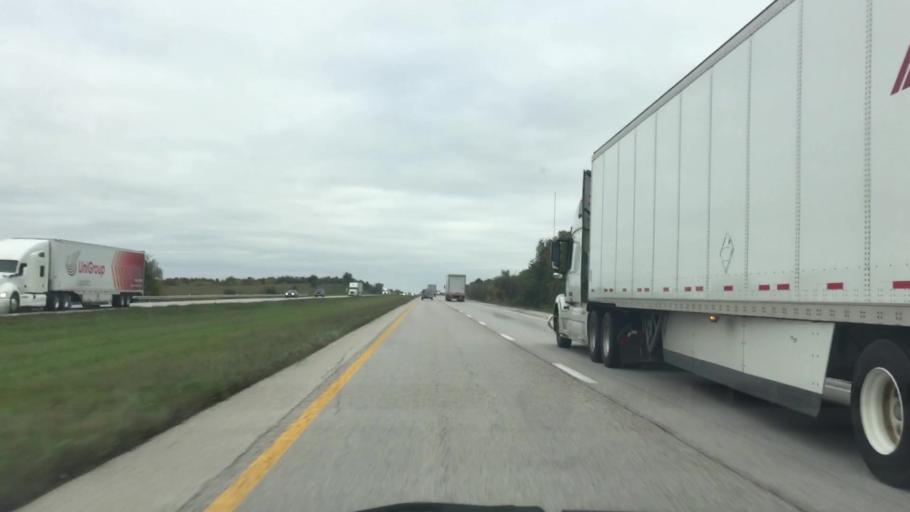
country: US
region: Missouri
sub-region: Clinton County
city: Cameron
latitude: 39.7044
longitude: -94.2265
